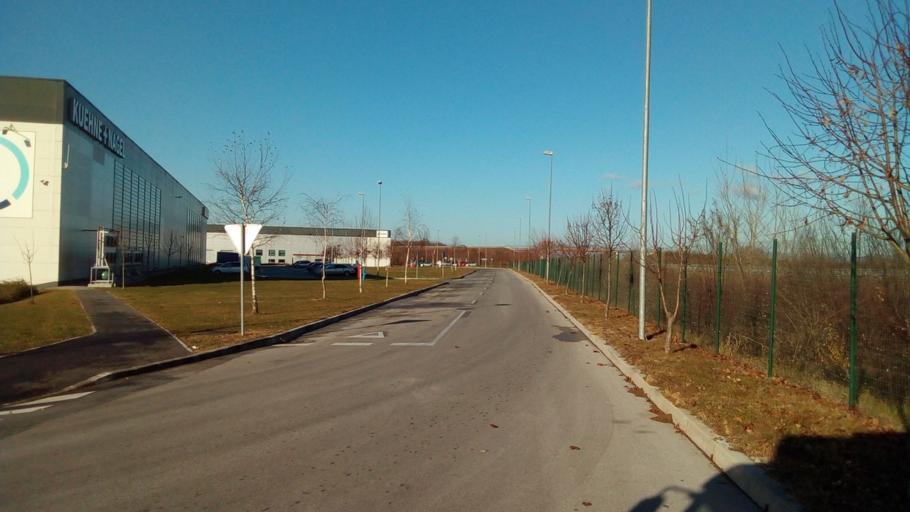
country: HR
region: Zagrebacka
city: Bestovje
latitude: 45.8046
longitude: 15.7747
